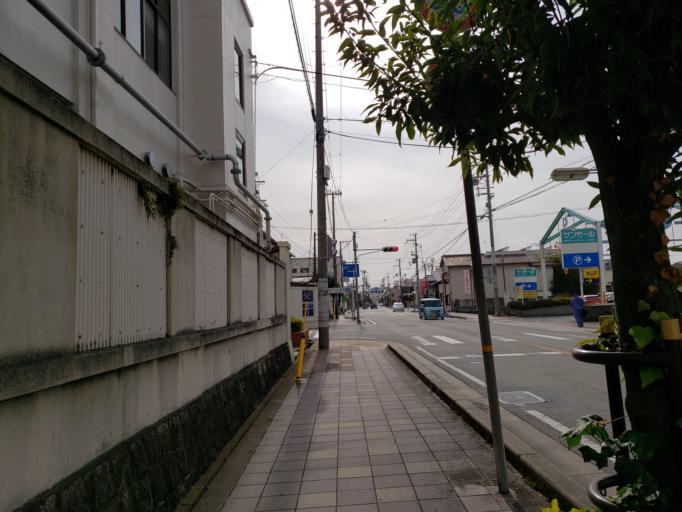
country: JP
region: Hyogo
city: Kakogawacho-honmachi
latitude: 34.7497
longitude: 134.8038
